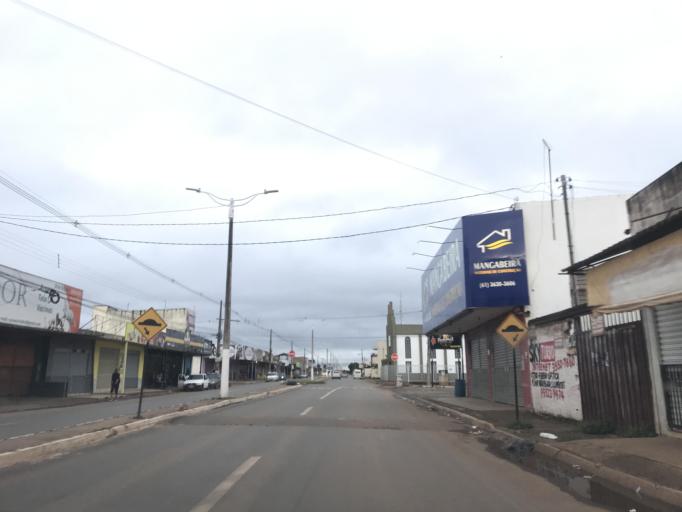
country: BR
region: Goias
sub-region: Luziania
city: Luziania
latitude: -16.2054
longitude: -47.9251
